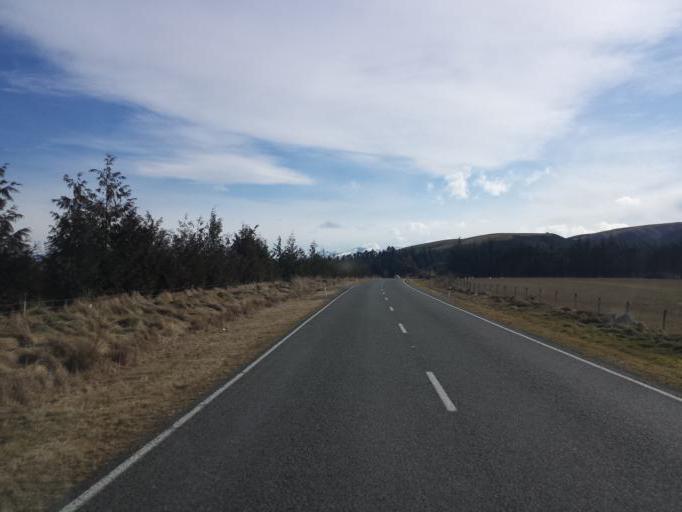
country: NZ
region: Canterbury
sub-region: Timaru District
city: Pleasant Point
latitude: -44.0882
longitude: 170.9881
